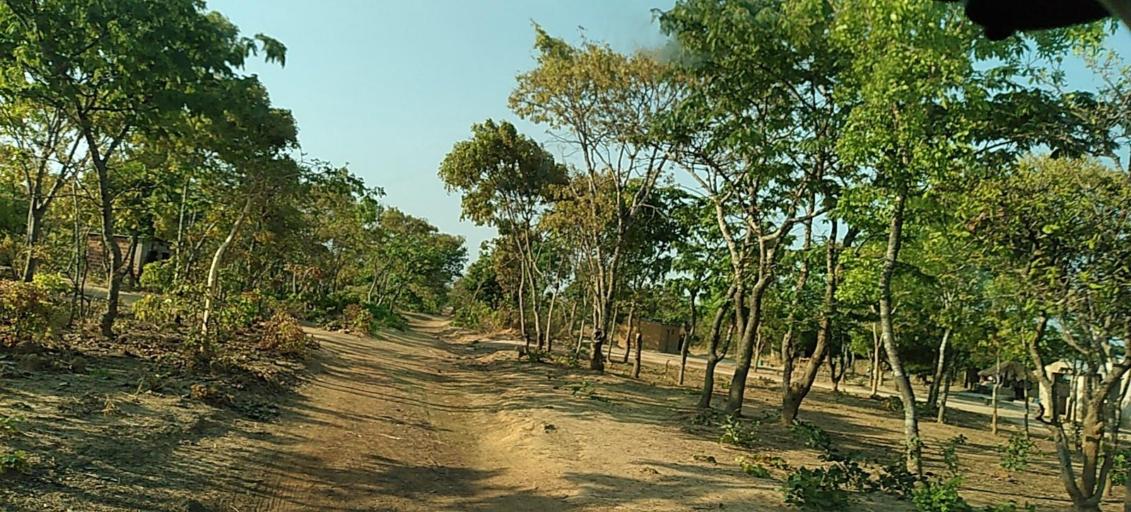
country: ZM
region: North-Western
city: Kalengwa
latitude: -13.1550
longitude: 25.0339
